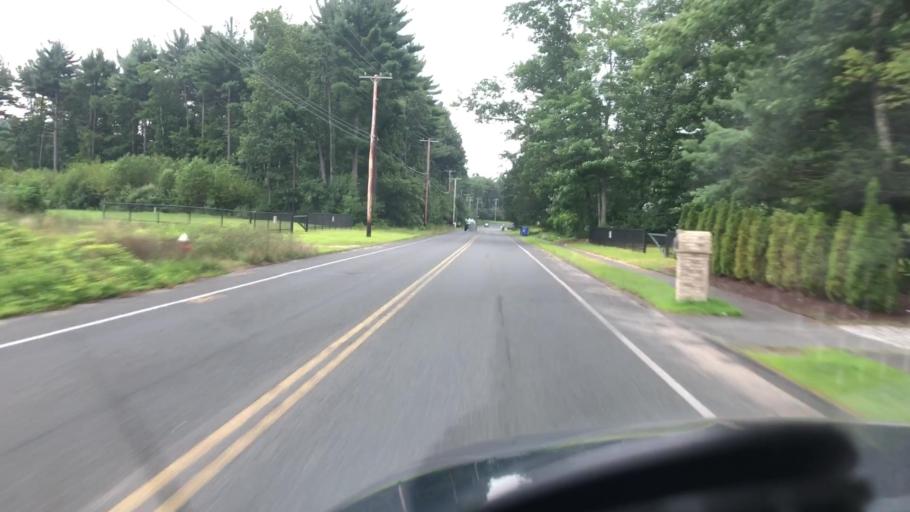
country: US
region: Massachusetts
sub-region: Hampshire County
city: Southampton
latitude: 42.1922
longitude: -72.6868
